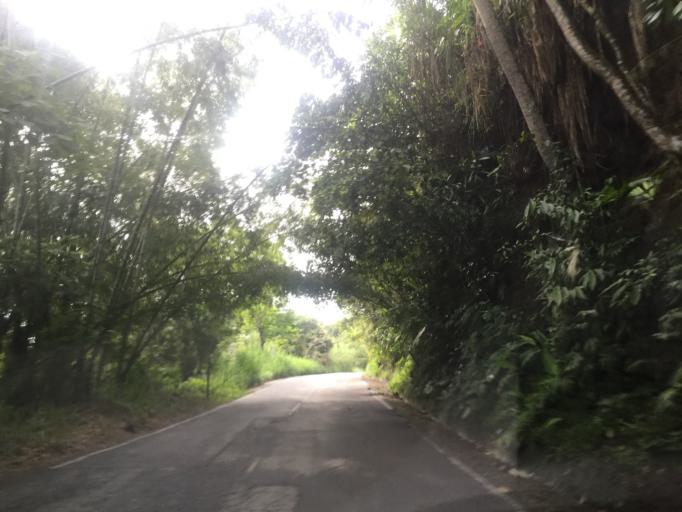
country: CO
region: Quindio
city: La Tebaida
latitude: 4.4649
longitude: -75.8067
